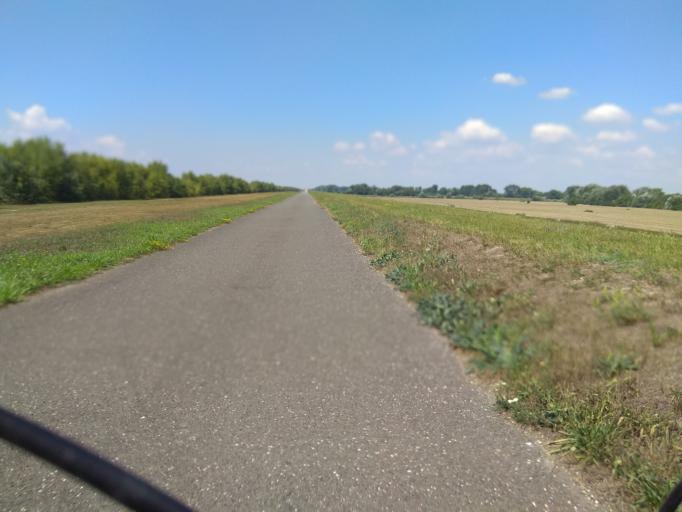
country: SK
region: Trnavsky
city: Gabcikovo
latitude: 47.8271
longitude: 17.6053
